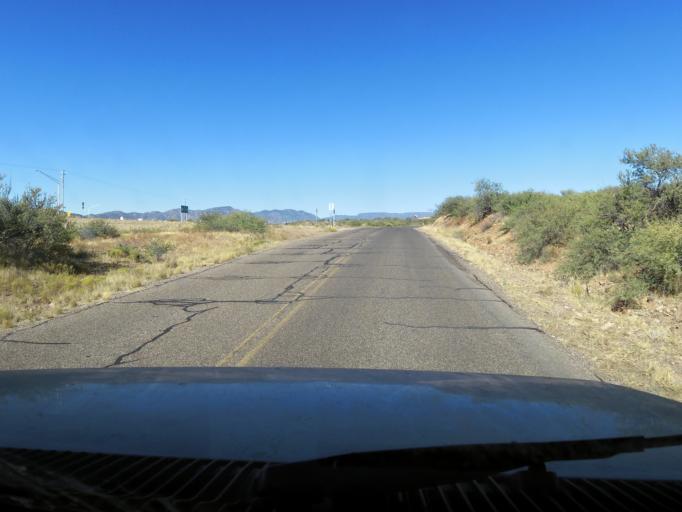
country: US
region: Arizona
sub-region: Yavapai County
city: Camp Verde
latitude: 34.5991
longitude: -111.8960
